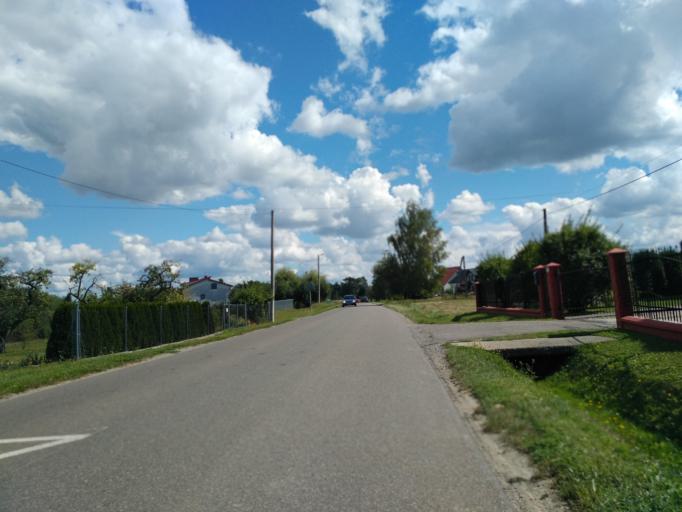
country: PL
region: Subcarpathian Voivodeship
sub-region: Powiat jasielski
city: Trzcinica
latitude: 49.7530
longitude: 21.4195
